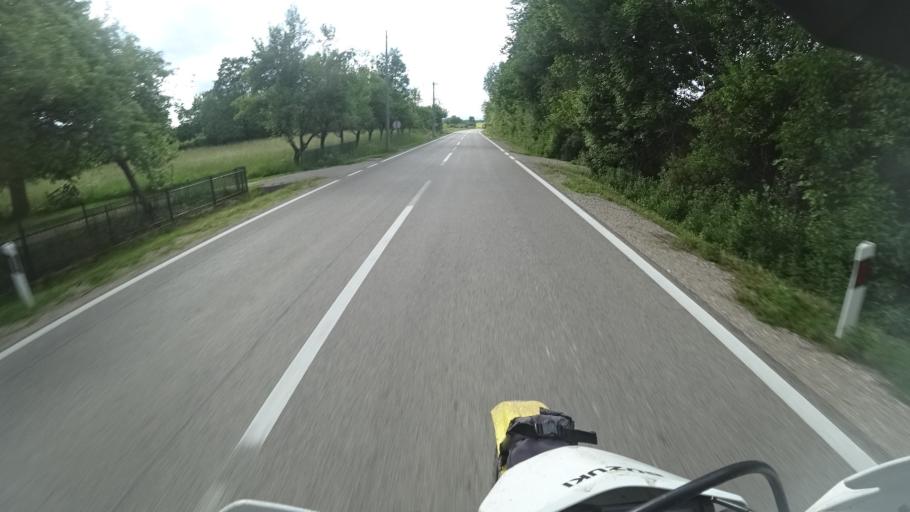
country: HR
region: Licko-Senjska
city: Gospic
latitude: 44.4992
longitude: 15.4549
